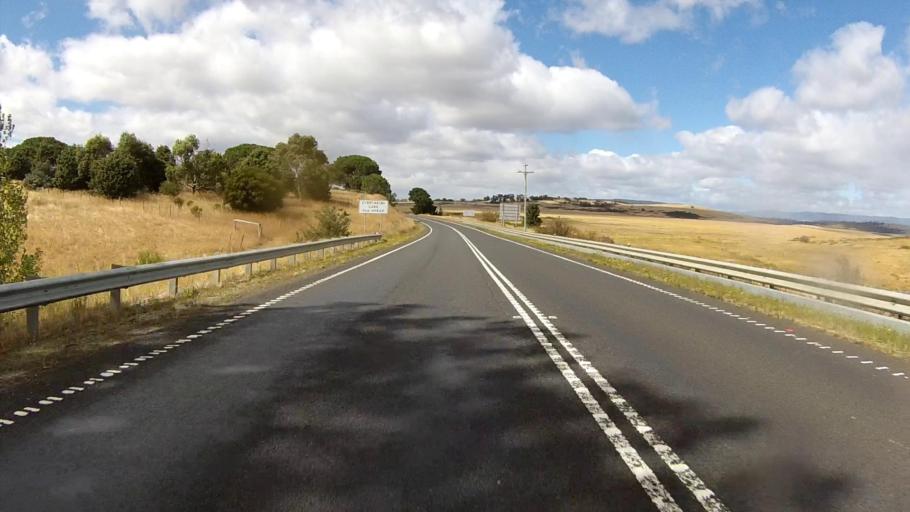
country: AU
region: Tasmania
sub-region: Northern Midlands
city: Evandale
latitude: -41.8421
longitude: 147.4481
